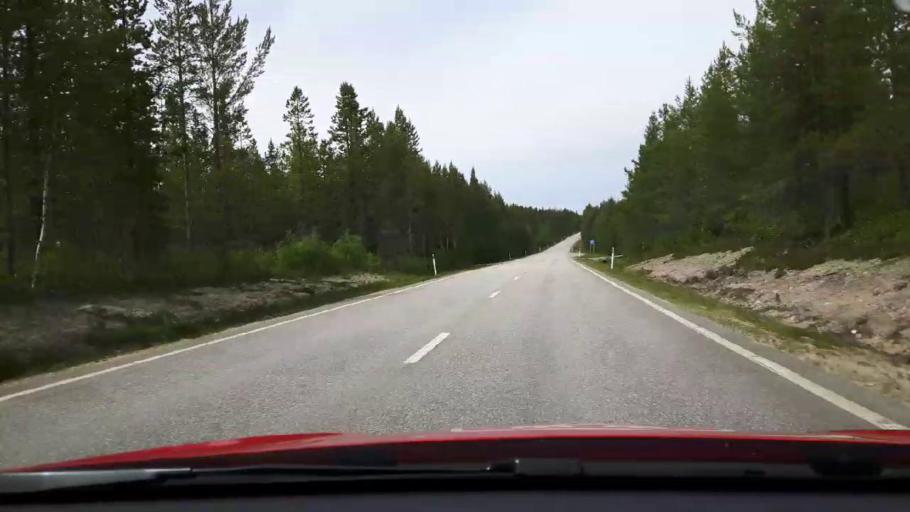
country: SE
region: Jaemtland
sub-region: Harjedalens Kommun
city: Sveg
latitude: 62.1099
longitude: 14.1891
